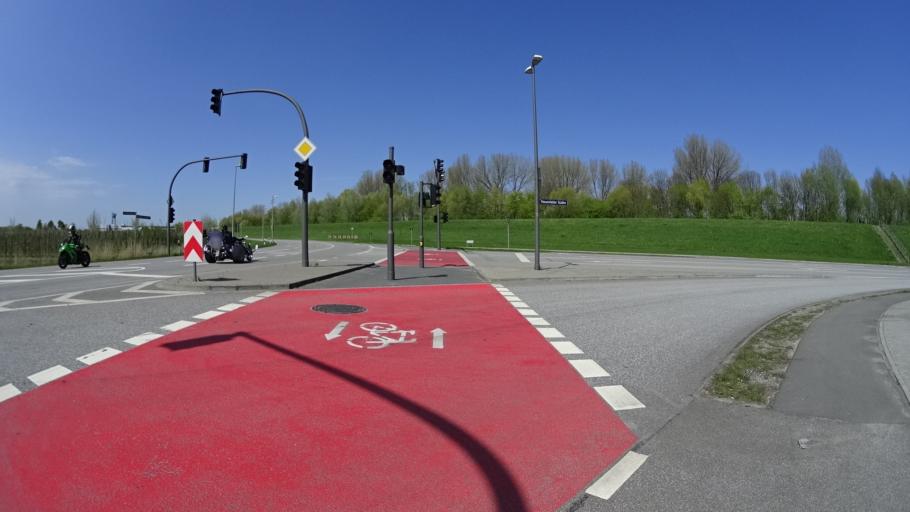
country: DE
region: Lower Saxony
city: Neu Wulmstorf
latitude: 53.5286
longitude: 9.8107
